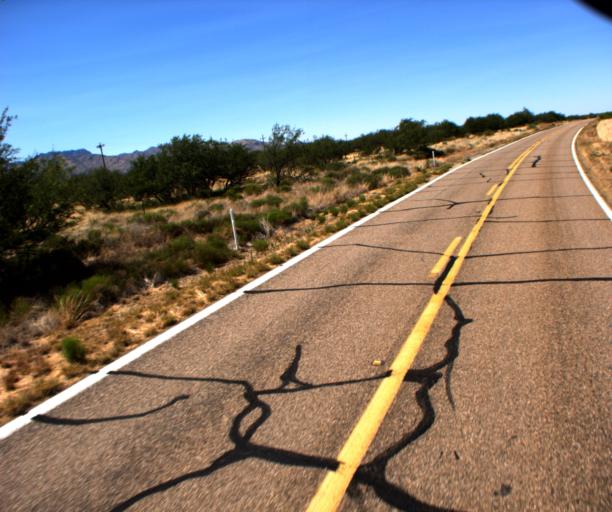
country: US
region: Arizona
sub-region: Pima County
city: Arivaca Junction
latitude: 31.6755
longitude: -111.4877
